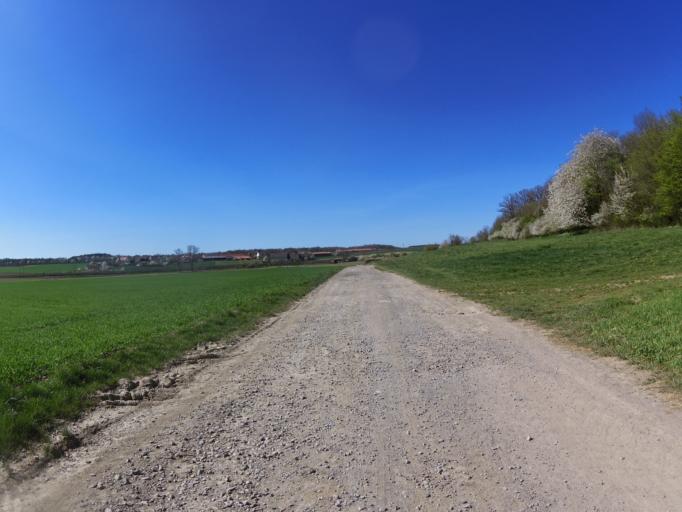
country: DE
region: Bavaria
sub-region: Regierungsbezirk Unterfranken
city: Rottendorf
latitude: 49.8084
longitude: 10.0646
